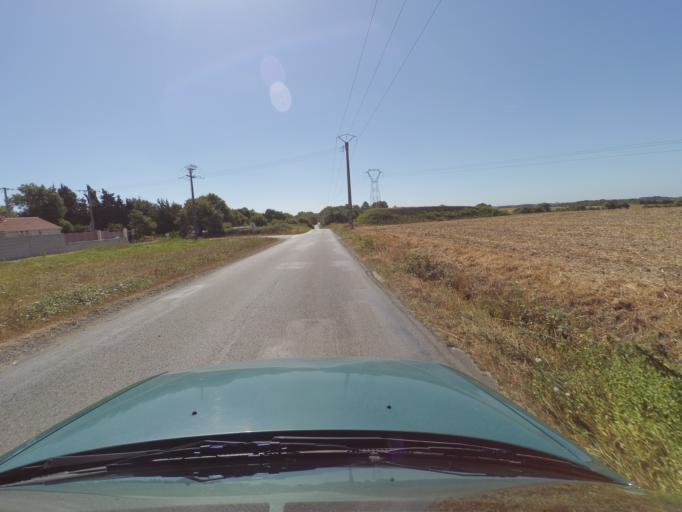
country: FR
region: Pays de la Loire
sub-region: Departement de la Loire-Atlantique
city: Les Sorinieres
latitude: 47.1283
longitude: -1.5141
